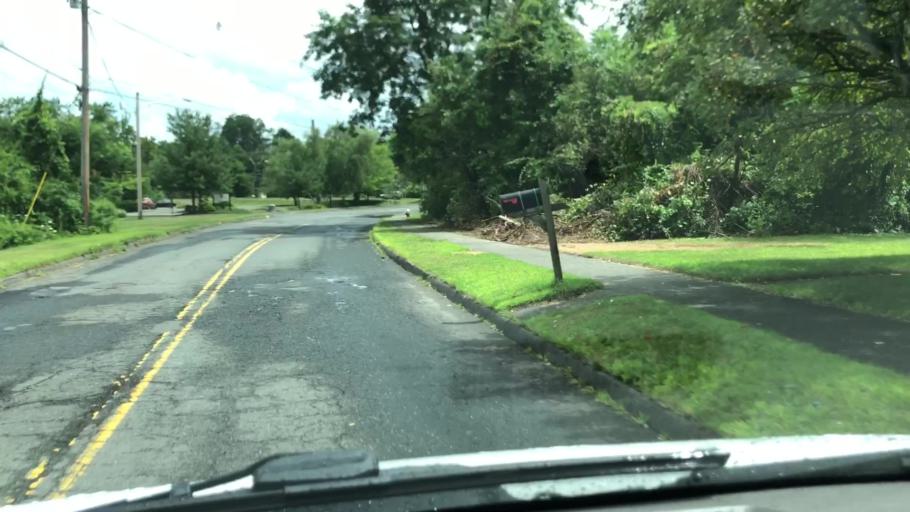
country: US
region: Massachusetts
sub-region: Hampshire County
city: Northampton
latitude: 42.3318
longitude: -72.6809
